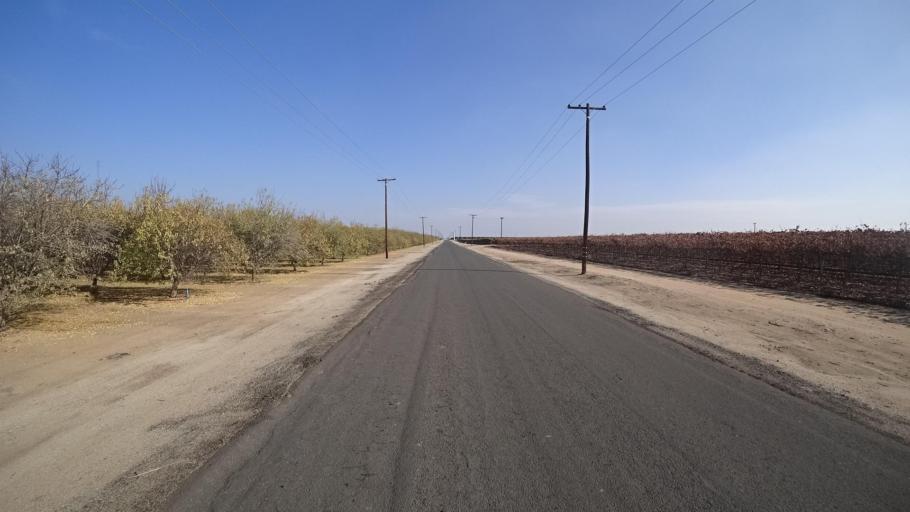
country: US
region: California
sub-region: Kern County
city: McFarland
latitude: 35.6311
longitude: -119.1834
